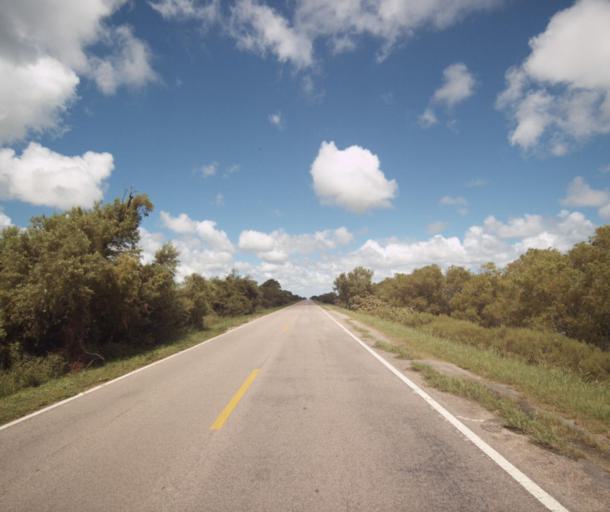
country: BR
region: Rio Grande do Sul
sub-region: Arroio Grande
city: Arroio Grande
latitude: -32.5492
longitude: -52.5454
